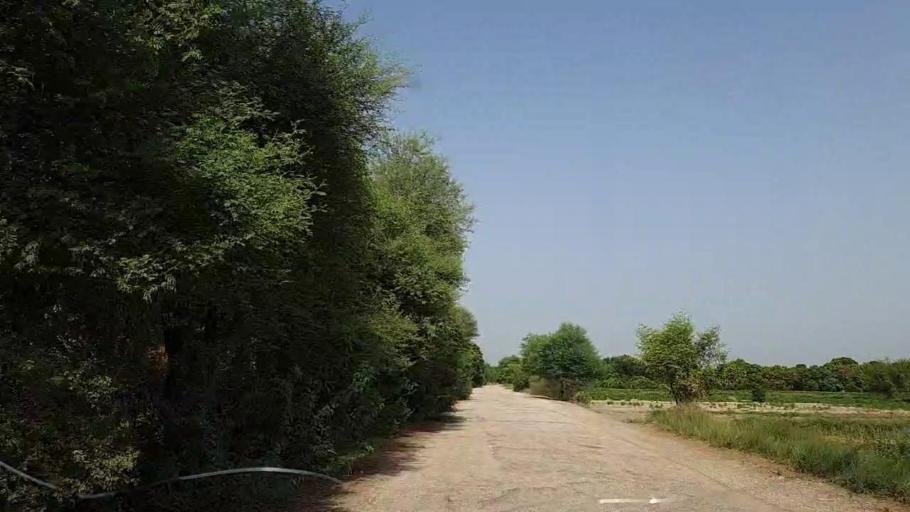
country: PK
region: Sindh
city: Kandiaro
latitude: 27.0648
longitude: 68.1948
